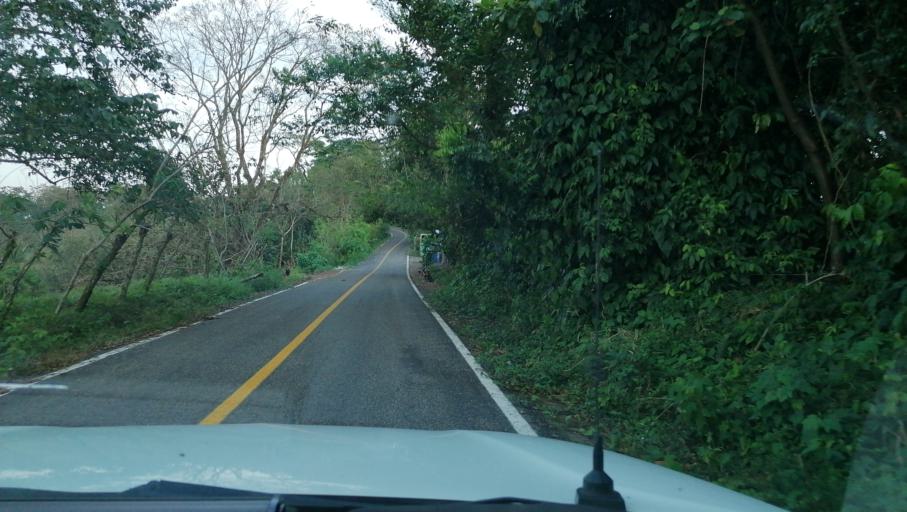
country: MX
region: Chiapas
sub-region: Juarez
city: El Triunfo 1ra. Seccion (Cardona)
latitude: 17.5055
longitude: -93.2220
